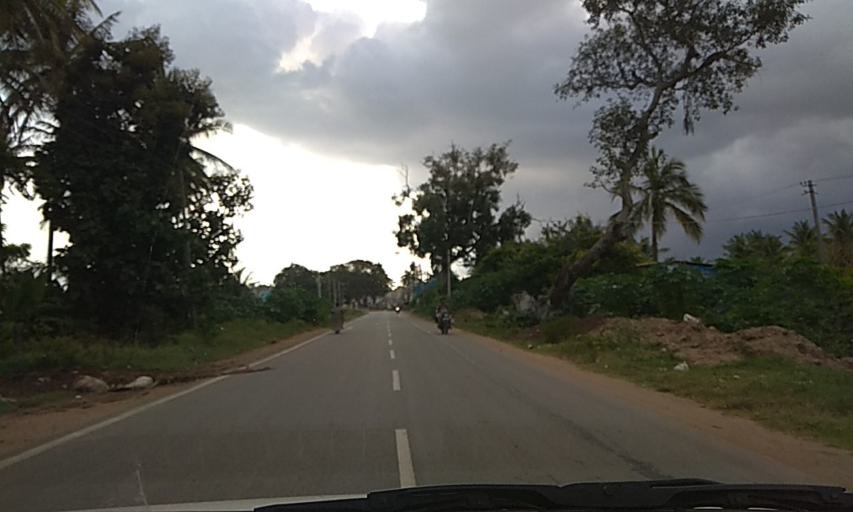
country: IN
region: Karnataka
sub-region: Chamrajnagar
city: Gundlupet
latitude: 11.8098
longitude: 76.6980
